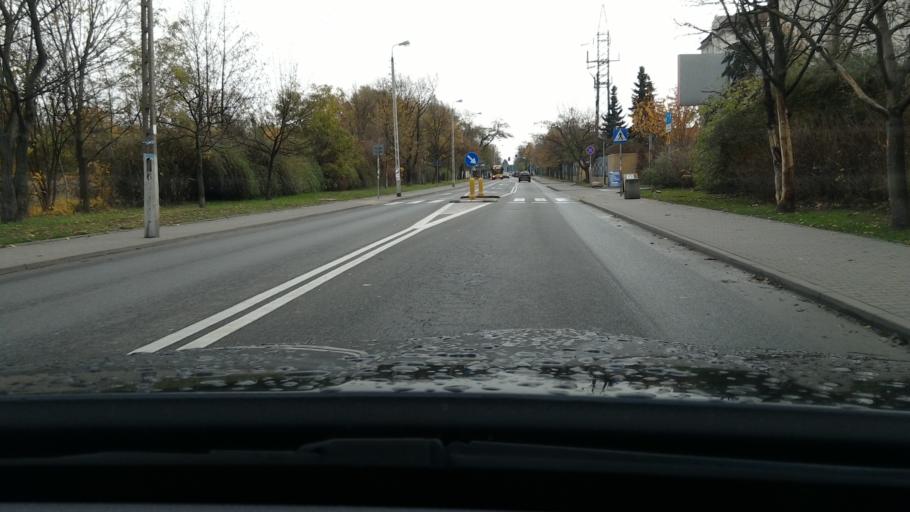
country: PL
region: Masovian Voivodeship
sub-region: Warszawa
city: Ursus
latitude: 52.1932
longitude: 20.9047
